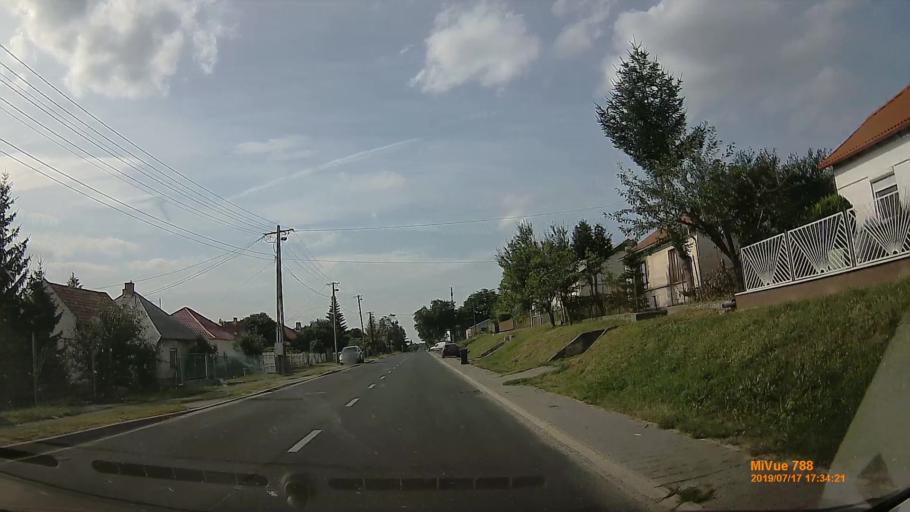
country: HU
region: Veszprem
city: Ajka
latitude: 47.0559
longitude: 17.5551
